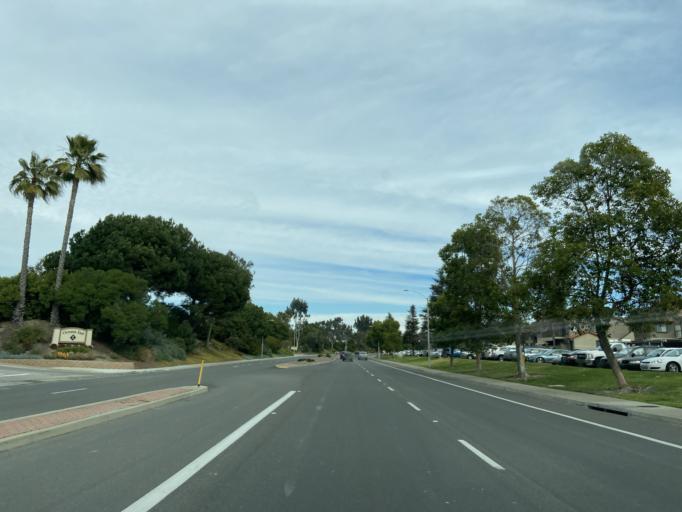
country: US
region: California
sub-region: San Diego County
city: Camp Pendleton South
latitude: 33.2126
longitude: -117.3212
